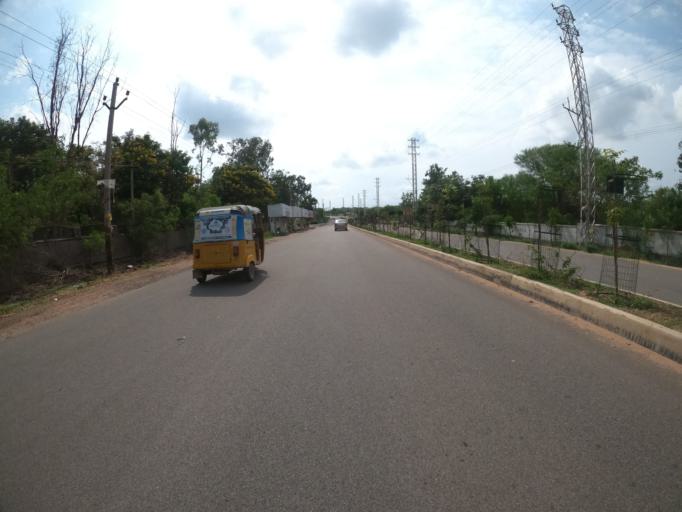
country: IN
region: Telangana
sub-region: Medak
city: Serilingampalle
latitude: 17.3933
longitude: 78.3207
